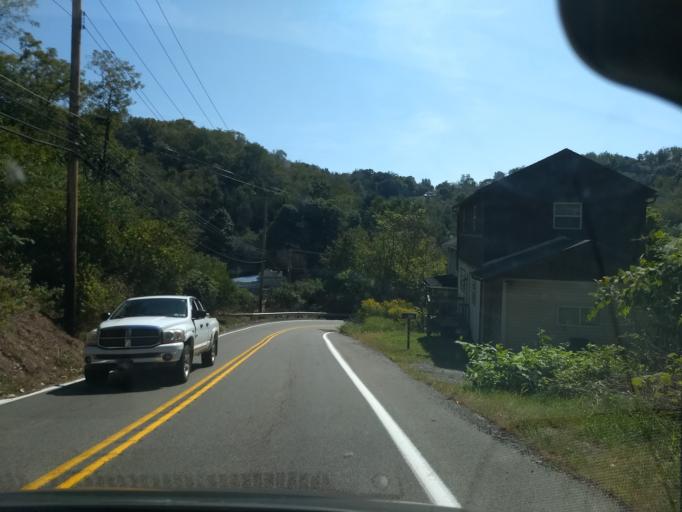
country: US
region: Pennsylvania
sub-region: Allegheny County
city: North Versailles
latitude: 40.3635
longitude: -79.8263
